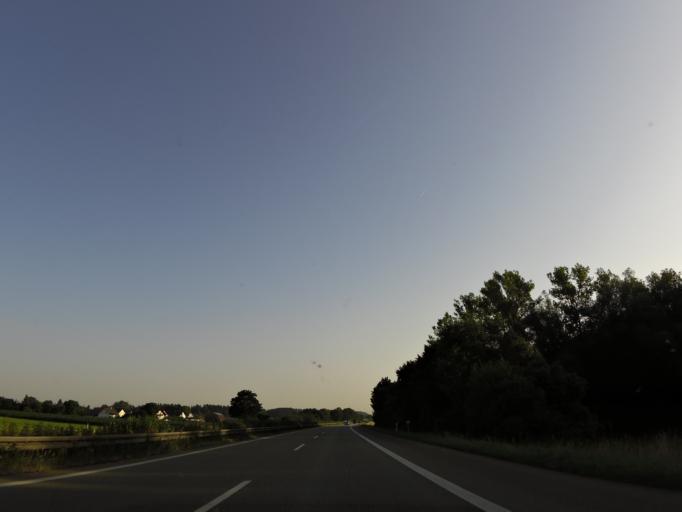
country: DE
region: Bavaria
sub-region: Swabia
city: Illertissen
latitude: 48.1970
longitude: 10.1230
